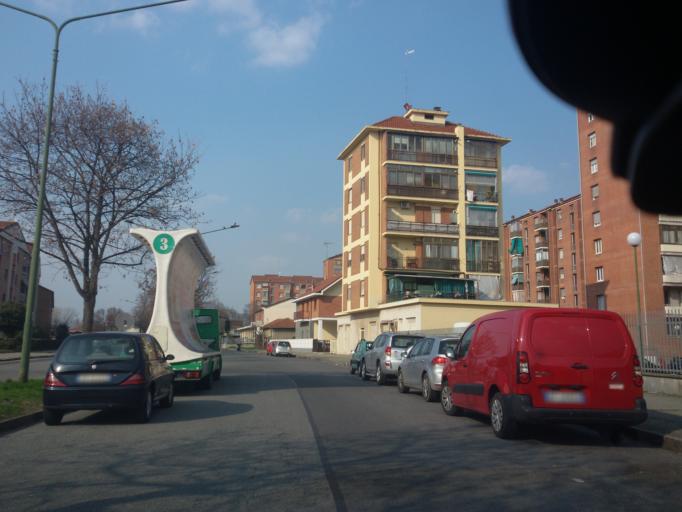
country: IT
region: Piedmont
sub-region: Provincia di Torino
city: Venaria Reale
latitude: 45.1040
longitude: 7.6361
